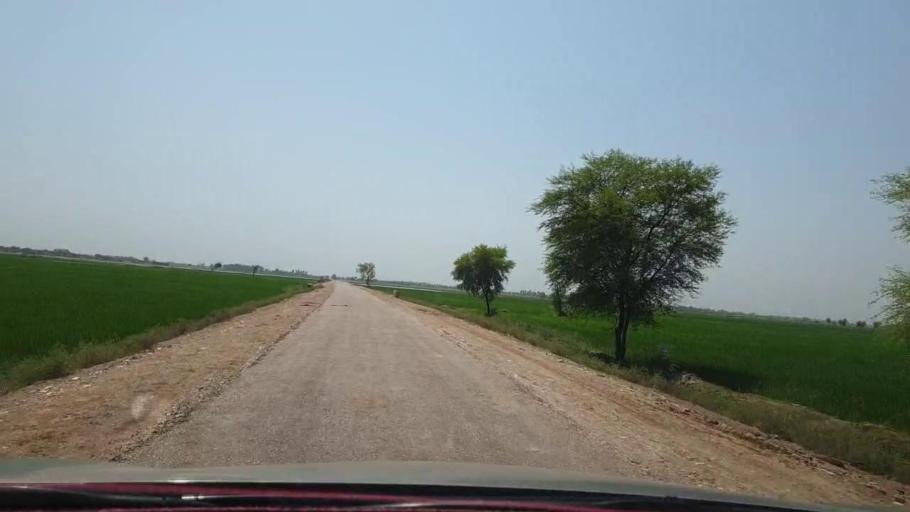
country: PK
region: Sindh
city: Warah
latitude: 27.5544
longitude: 67.7974
